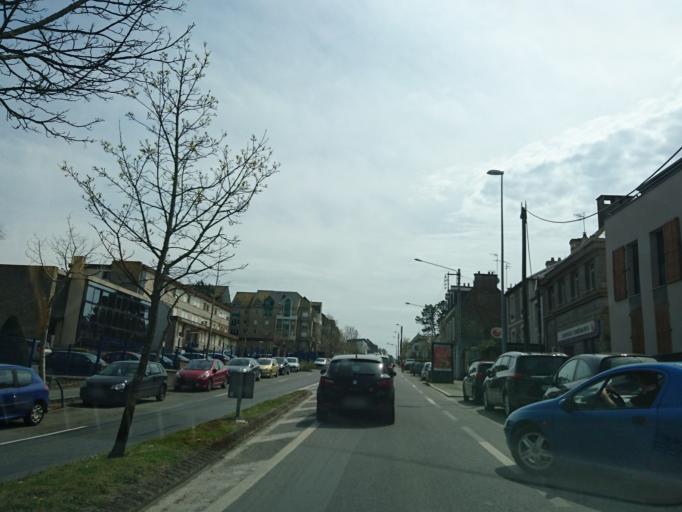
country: FR
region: Brittany
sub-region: Departement d'Ille-et-Vilaine
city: Saint-Malo
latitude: 48.6369
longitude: -2.0096
